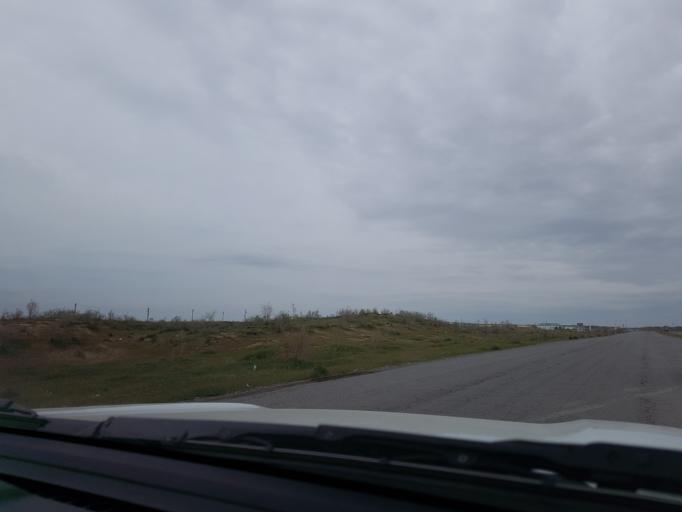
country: TM
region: Mary
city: Bayramaly
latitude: 38.0978
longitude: 62.8010
